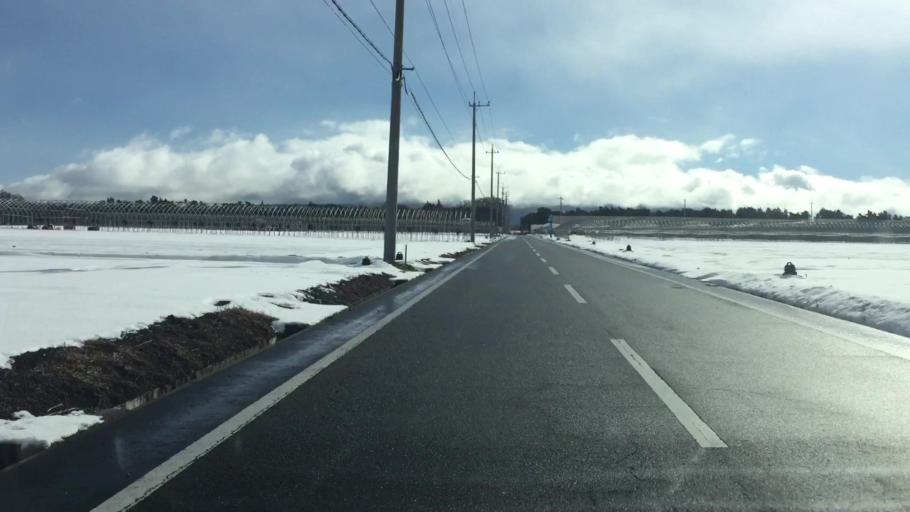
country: JP
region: Gunma
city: Numata
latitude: 36.6306
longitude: 139.0895
